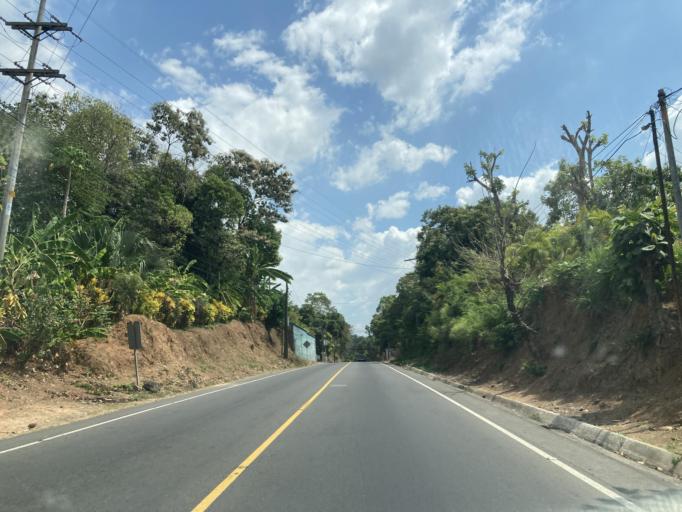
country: GT
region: Santa Rosa
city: Guazacapan
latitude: 14.0675
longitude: -90.4404
